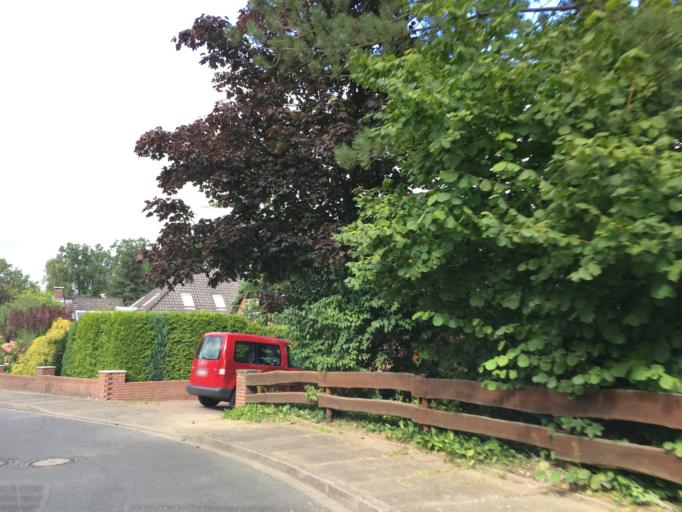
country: DE
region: Lower Saxony
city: Melbeck
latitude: 53.2151
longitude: 10.3936
